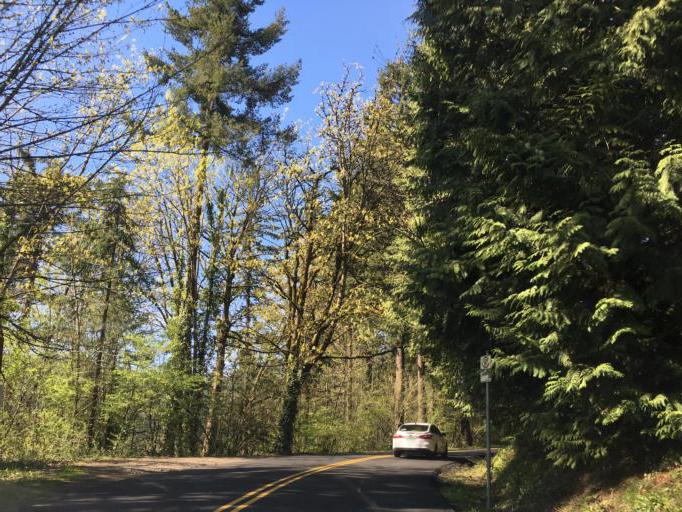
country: US
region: Oregon
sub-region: Multnomah County
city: Portland
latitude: 45.5113
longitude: -122.7125
